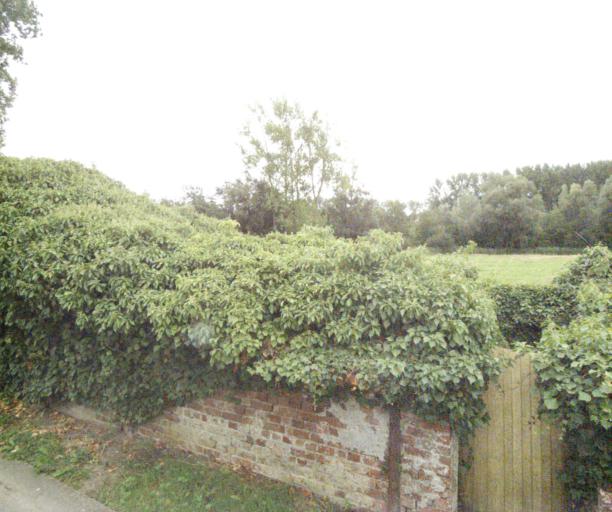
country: FR
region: Nord-Pas-de-Calais
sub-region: Departement du Nord
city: Fretin
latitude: 50.5594
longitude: 3.1641
